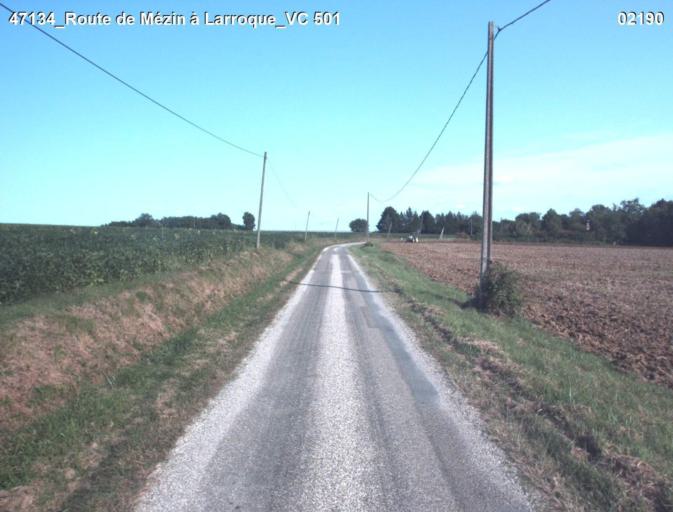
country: FR
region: Aquitaine
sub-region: Departement du Lot-et-Garonne
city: Mezin
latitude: 44.0168
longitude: 0.2770
